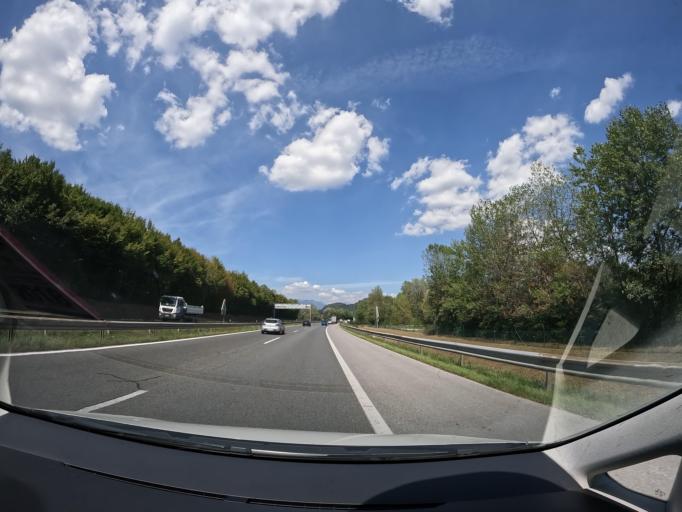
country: SI
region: Ljubljana
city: Ljubljana
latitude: 46.1023
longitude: 14.4769
